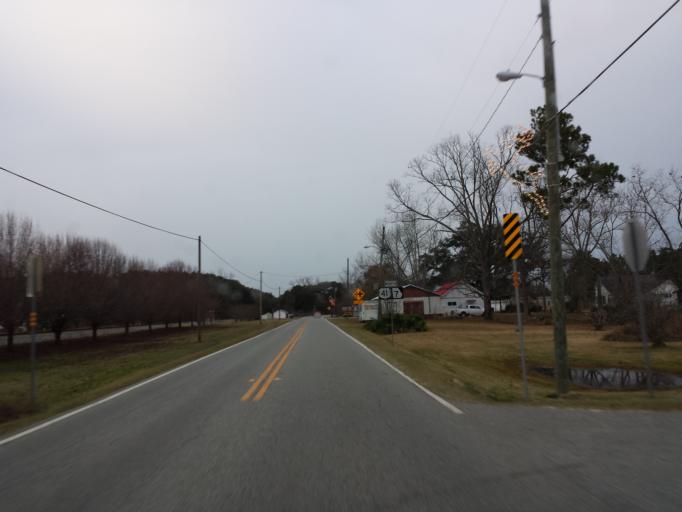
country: US
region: Georgia
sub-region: Lowndes County
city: Hahira
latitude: 31.0467
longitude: -83.3929
